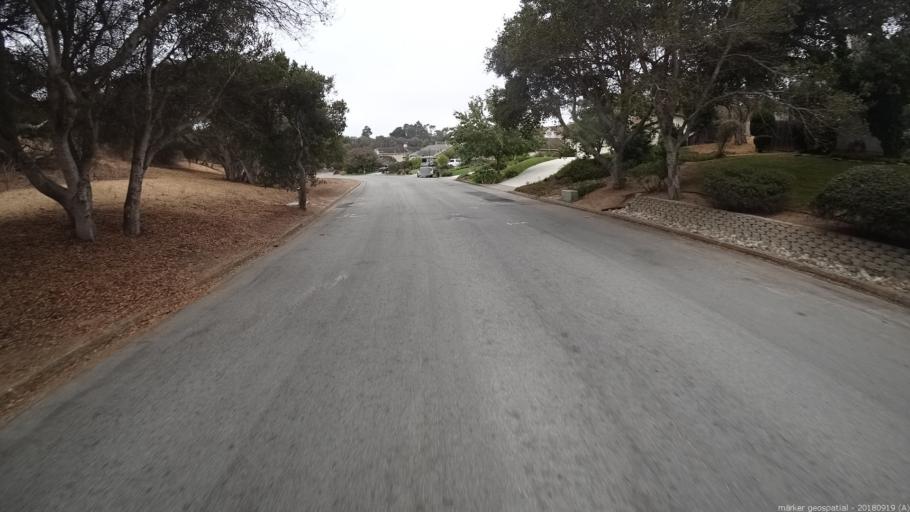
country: US
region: California
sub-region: Monterey County
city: Prunedale
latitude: 36.7798
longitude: -121.7143
